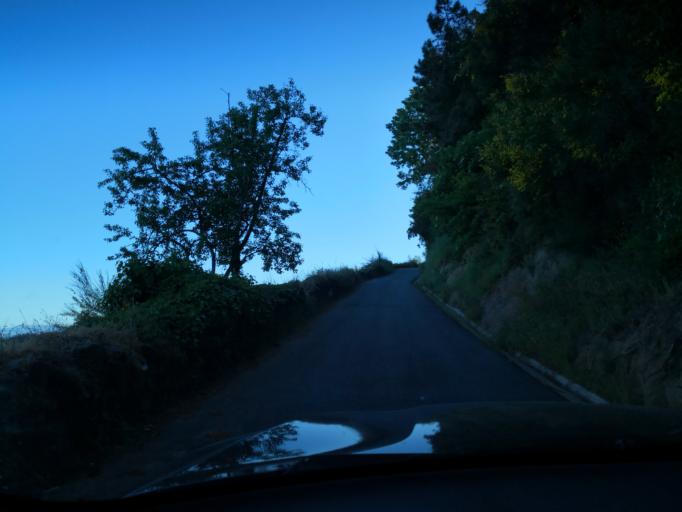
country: PT
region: Vila Real
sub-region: Vila Real
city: Vila Real
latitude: 41.3315
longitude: -7.7467
